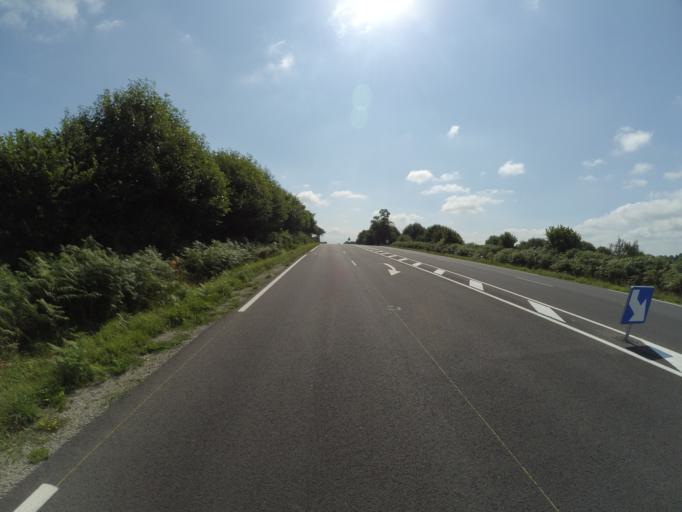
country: FR
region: Brittany
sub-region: Departement du Finistere
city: Bannalec
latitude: 47.9395
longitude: -3.7500
